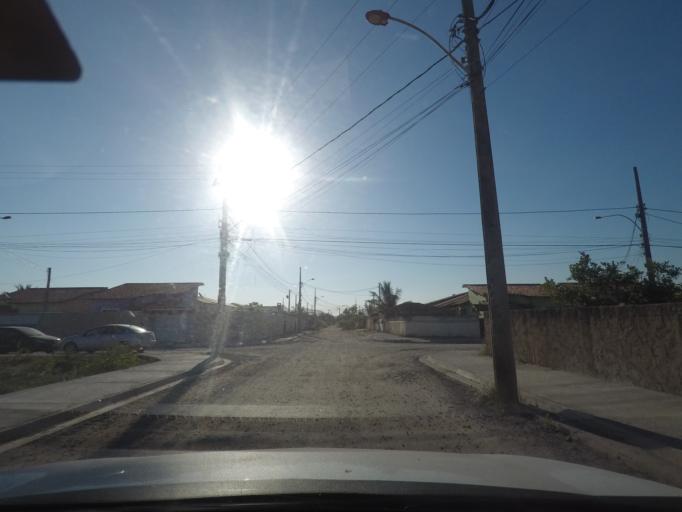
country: BR
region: Rio de Janeiro
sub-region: Marica
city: Marica
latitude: -22.9620
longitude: -42.9458
